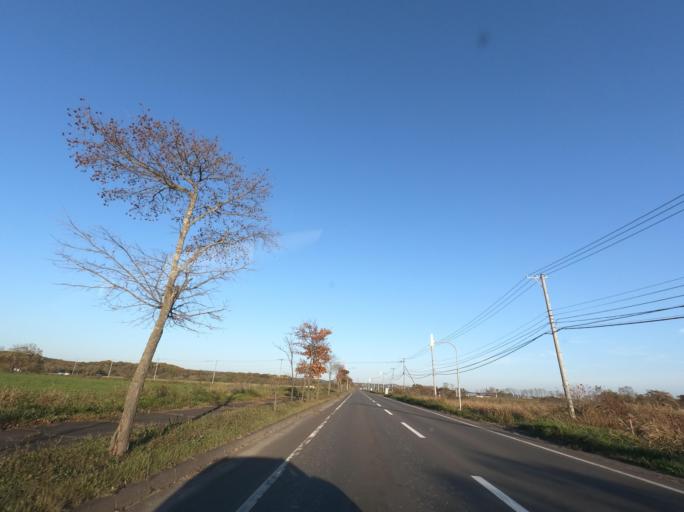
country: JP
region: Hokkaido
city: Kushiro
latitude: 43.0718
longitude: 144.2201
